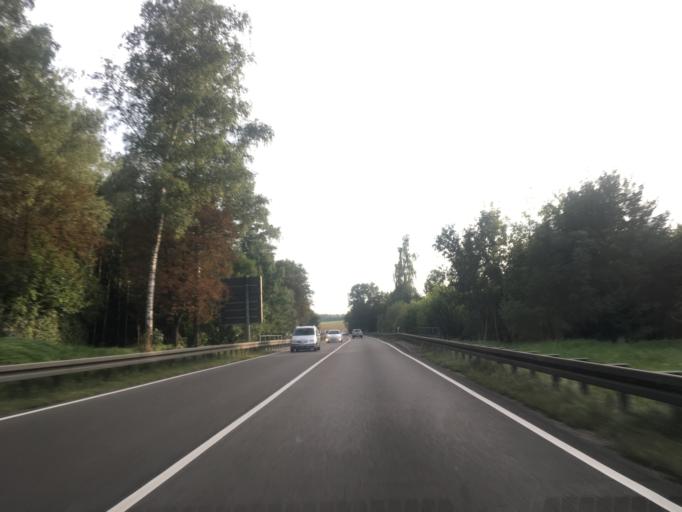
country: DE
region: Baden-Wuerttemberg
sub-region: Tuebingen Region
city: Metzingen
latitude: 48.5396
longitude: 9.2667
